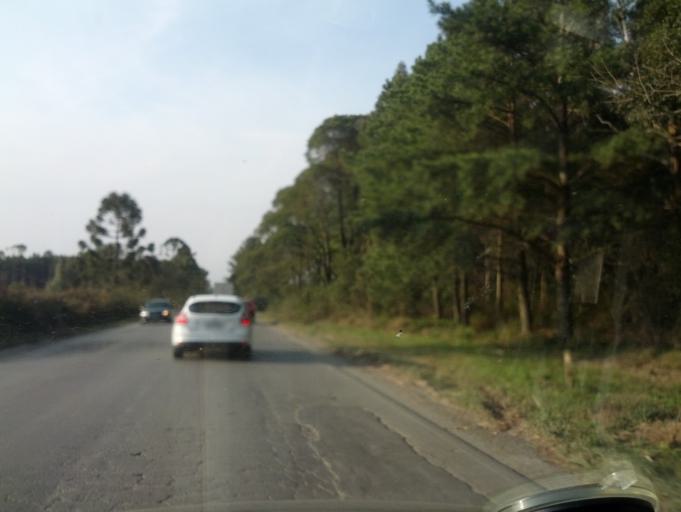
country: BR
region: Santa Catarina
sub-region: Otacilio Costa
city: Otacilio Costa
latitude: -27.5437
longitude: -50.1459
